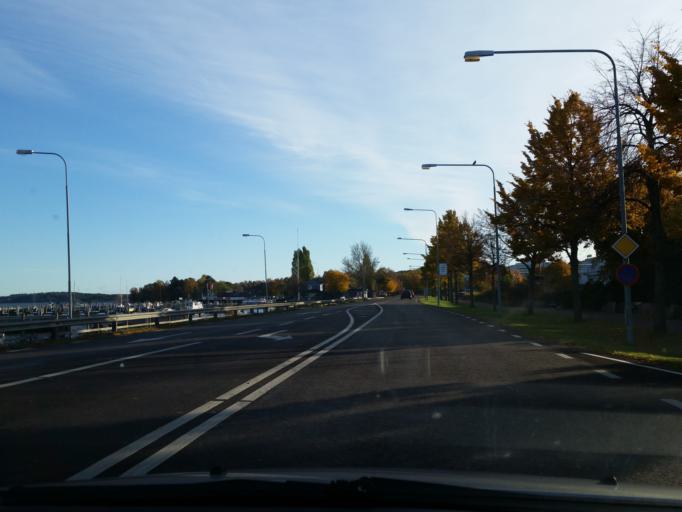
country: AX
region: Mariehamns stad
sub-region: Mariehamn
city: Mariehamn
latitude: 60.1022
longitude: 19.9451
